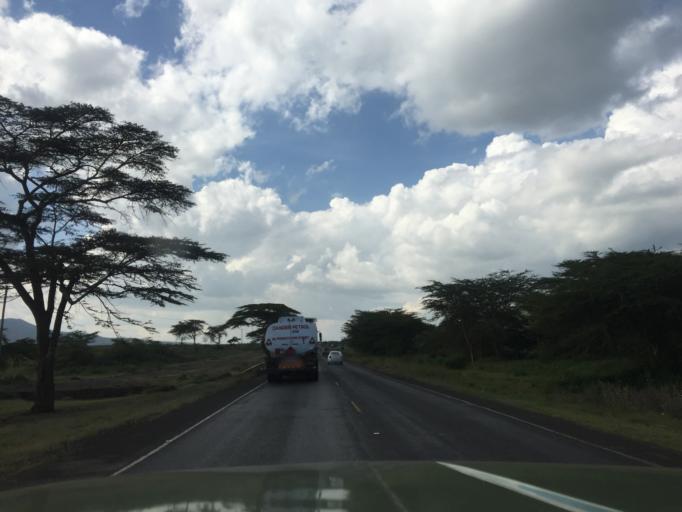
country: KE
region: Nakuru
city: Kijabe
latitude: -0.9464
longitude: 36.5467
